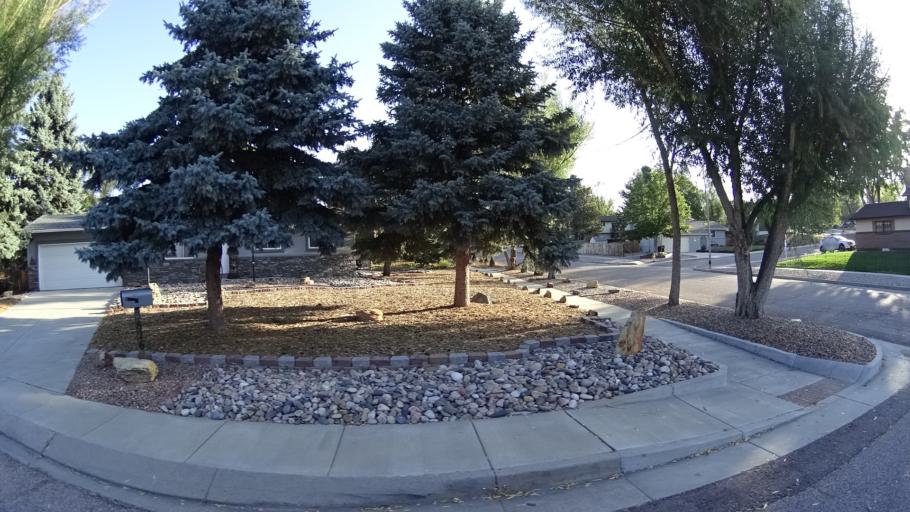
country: US
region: Colorado
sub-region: El Paso County
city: Cimarron Hills
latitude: 38.8865
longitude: -104.7540
